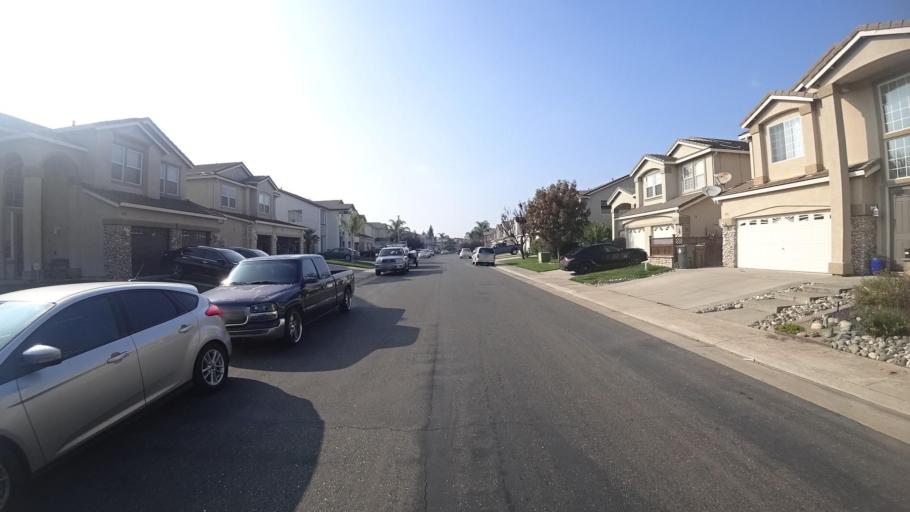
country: US
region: California
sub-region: Sacramento County
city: Elk Grove
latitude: 38.4180
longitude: -121.3445
